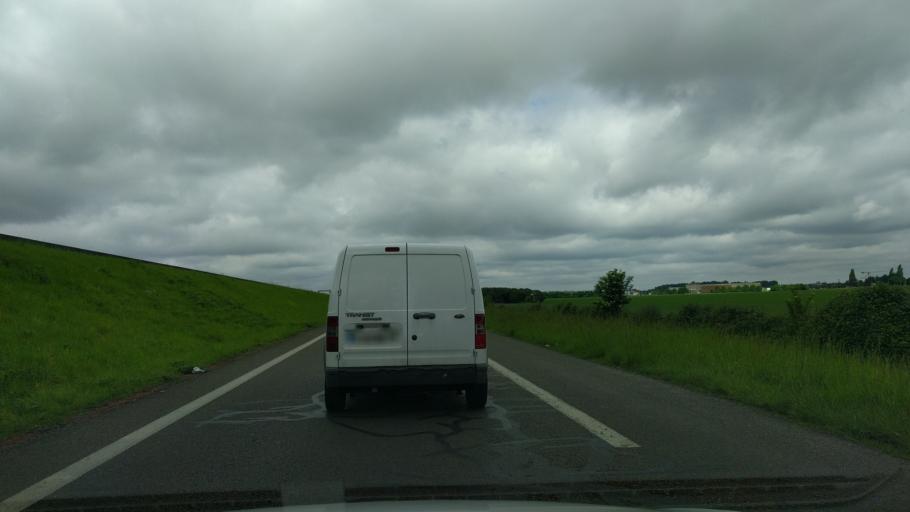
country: FR
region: Ile-de-France
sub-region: Departement de Seine-et-Marne
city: Nandy
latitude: 48.6108
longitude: 2.5744
